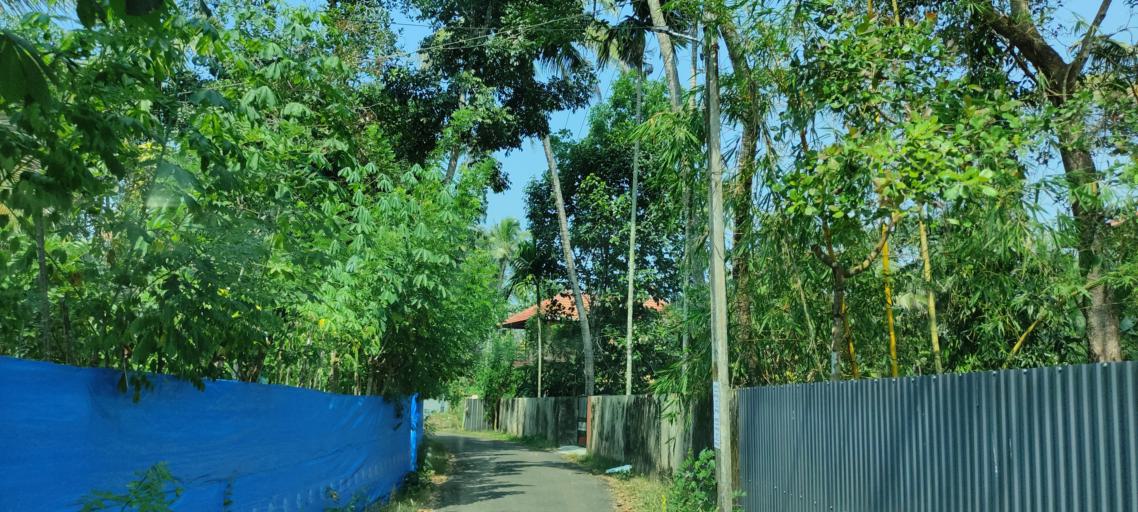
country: IN
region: Kerala
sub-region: Alappuzha
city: Shertallai
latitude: 9.6019
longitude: 76.3200
